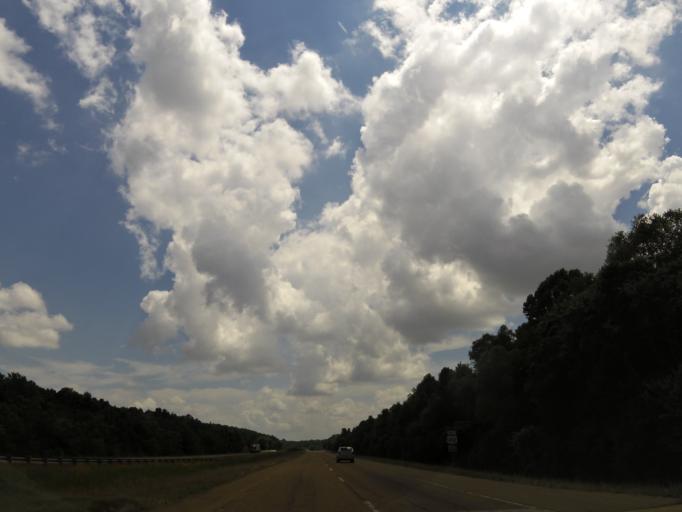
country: US
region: Tennessee
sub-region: Dyer County
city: Dyersburg
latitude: 35.9924
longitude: -89.3424
